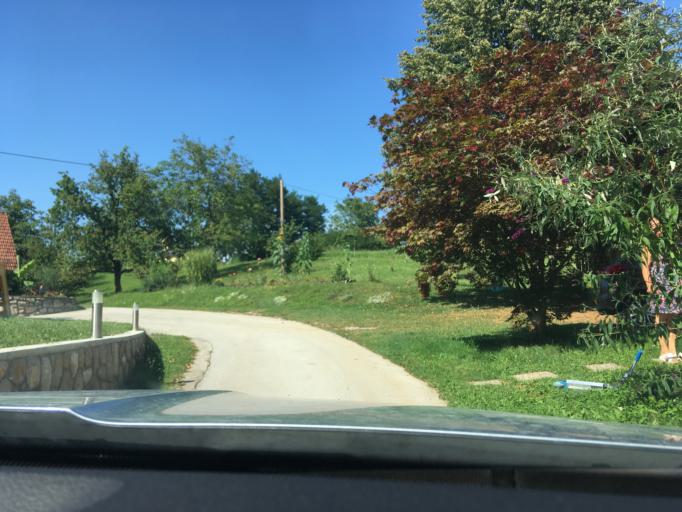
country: HR
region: Karlovacka
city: Ozalj
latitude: 45.4903
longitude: 15.3566
